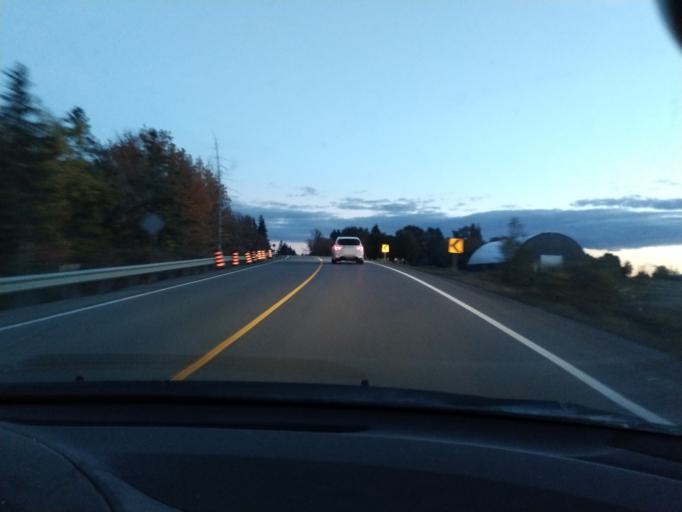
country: CA
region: Ontario
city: Bradford West Gwillimbury
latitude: 44.1546
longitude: -79.6538
